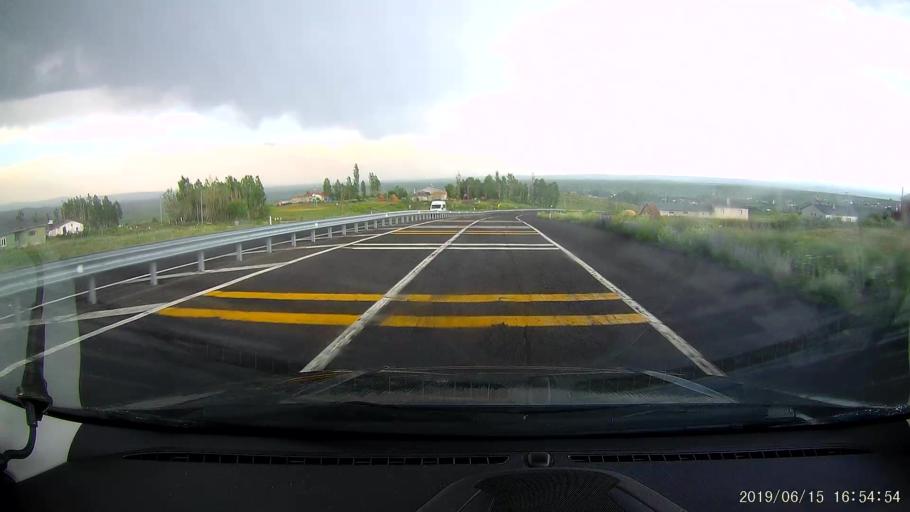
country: TR
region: Kars
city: Susuz
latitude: 40.7879
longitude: 43.1346
